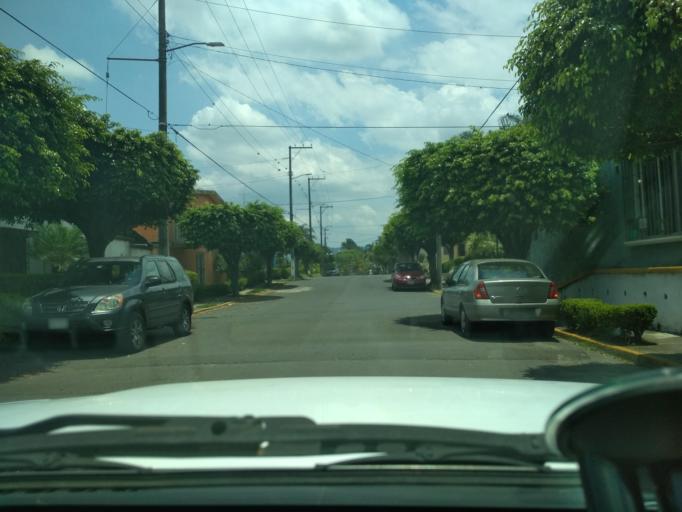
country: MX
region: Veracruz
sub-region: Cordoba
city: San Jose de Abajo [Unidad Habitacional]
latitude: 18.9110
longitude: -96.9595
